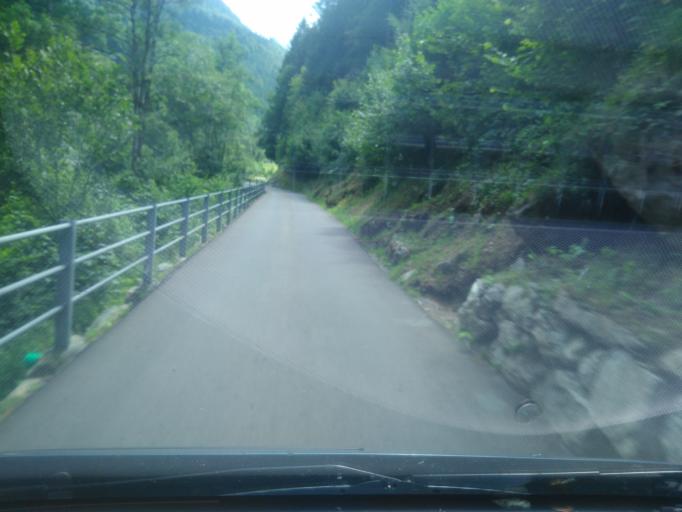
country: CH
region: Bern
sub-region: Interlaken-Oberhasli District
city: Meiringen
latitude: 46.6957
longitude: 8.2265
